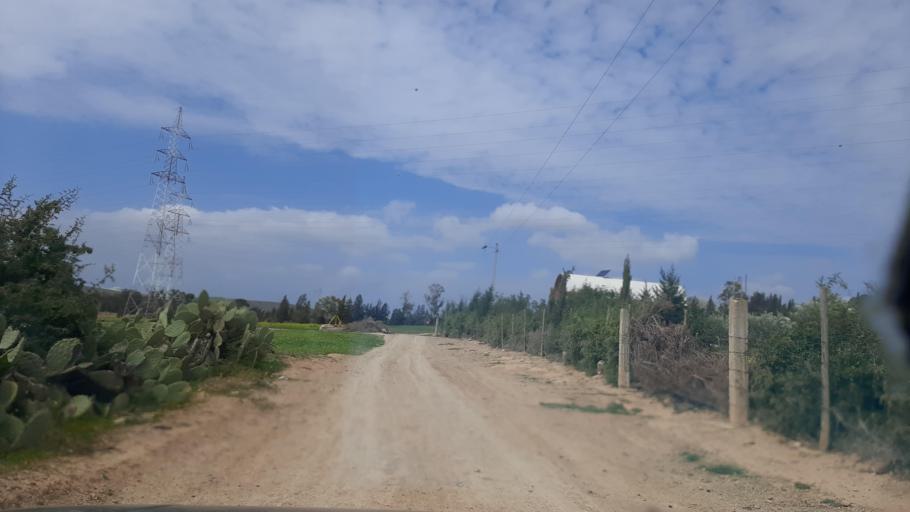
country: TN
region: Tunis
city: La Mohammedia
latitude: 36.6855
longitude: 10.0089
